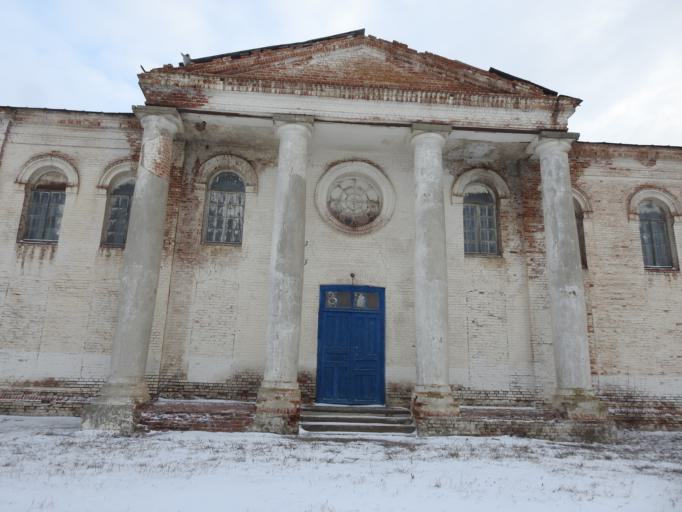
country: RU
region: Saratov
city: Krasnyy Yar
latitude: 51.5643
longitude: 46.5033
